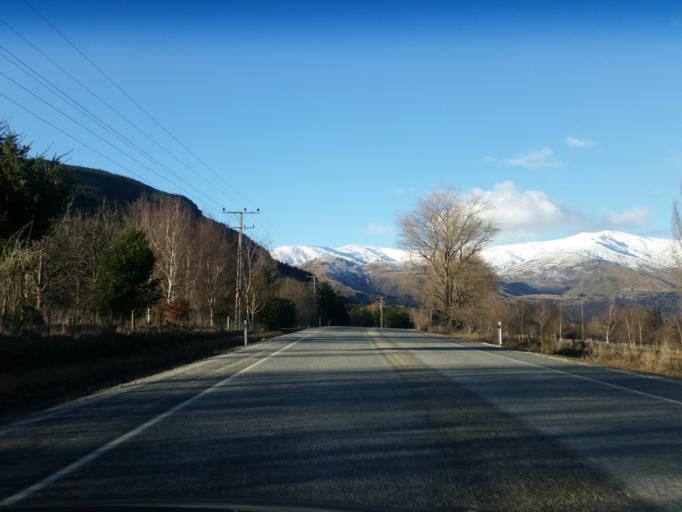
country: NZ
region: Otago
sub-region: Queenstown-Lakes District
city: Arrowtown
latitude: -44.9466
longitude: 168.7856
